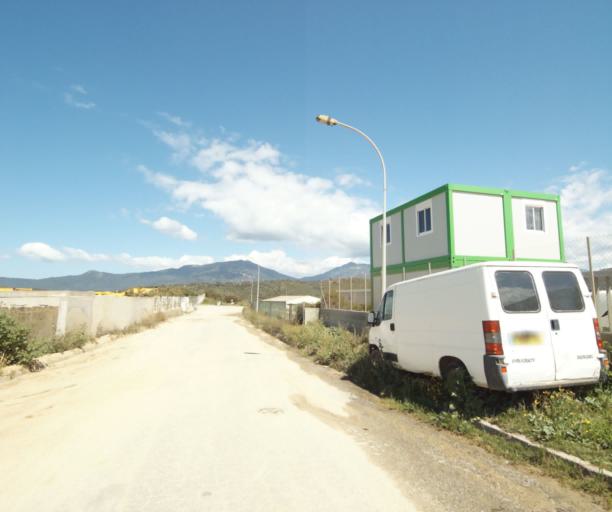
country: FR
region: Corsica
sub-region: Departement de la Corse-du-Sud
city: Propriano
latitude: 41.6553
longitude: 8.8992
